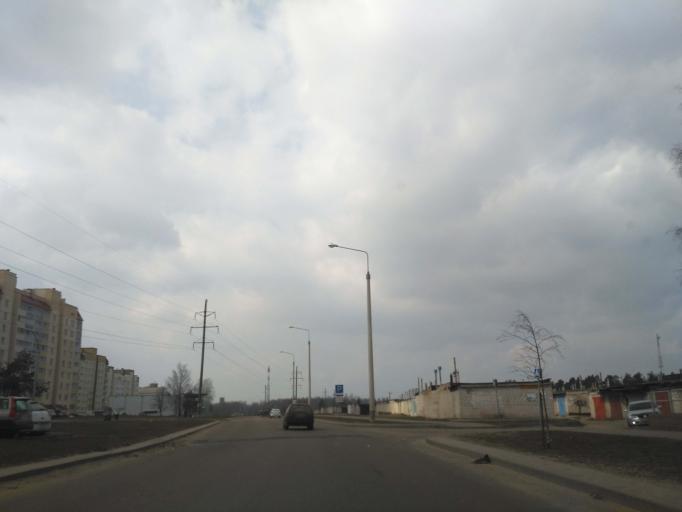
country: BY
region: Minsk
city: Horad Barysaw
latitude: 54.2160
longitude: 28.4758
